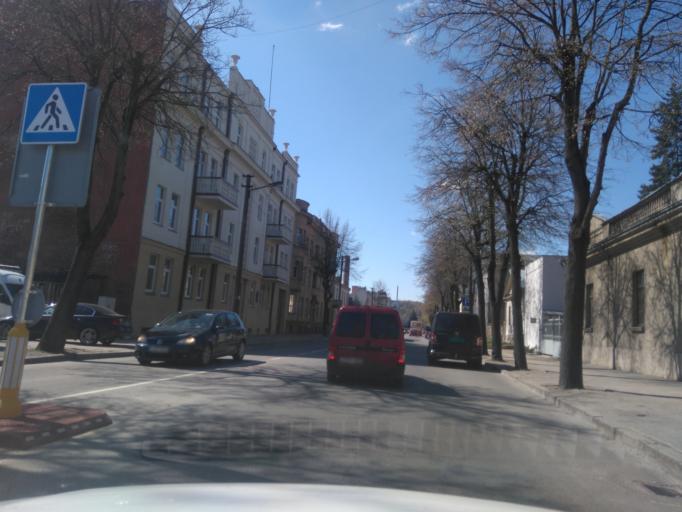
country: LT
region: Kauno apskritis
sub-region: Kaunas
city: Aleksotas
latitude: 54.8905
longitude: 23.9246
